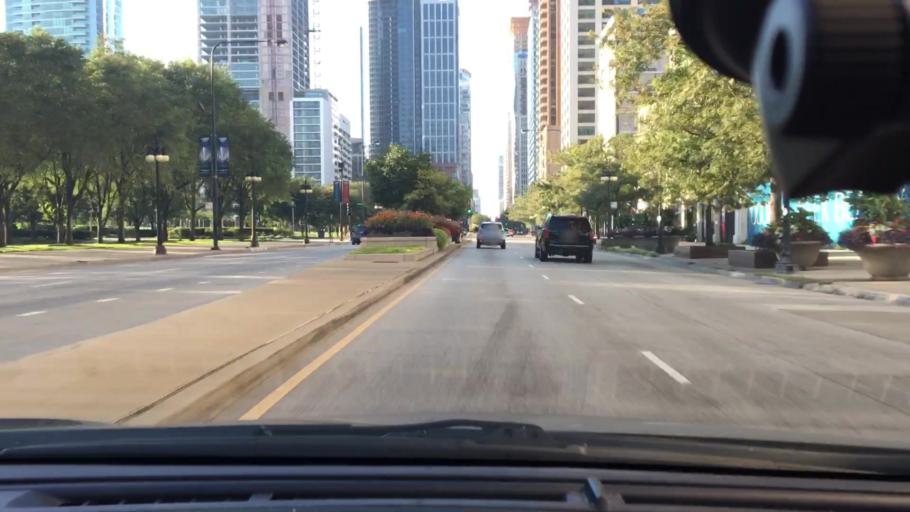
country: US
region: Illinois
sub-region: Cook County
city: Chicago
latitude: 41.8703
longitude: -87.6242
